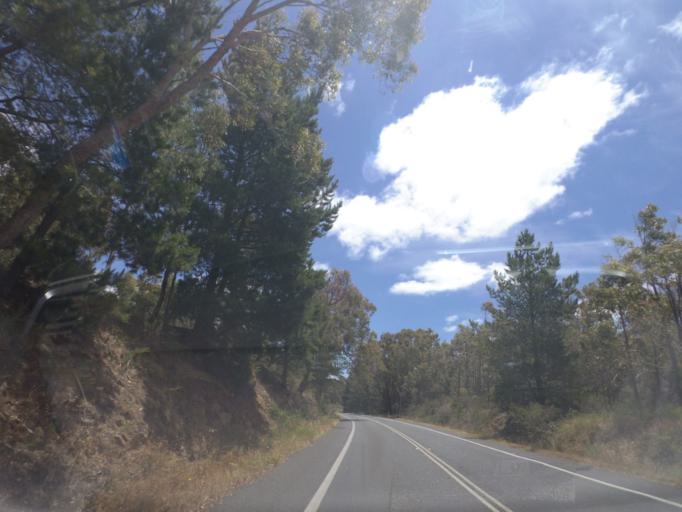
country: AU
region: Victoria
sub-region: Mount Alexander
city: Castlemaine
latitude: -37.2840
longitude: 144.1600
